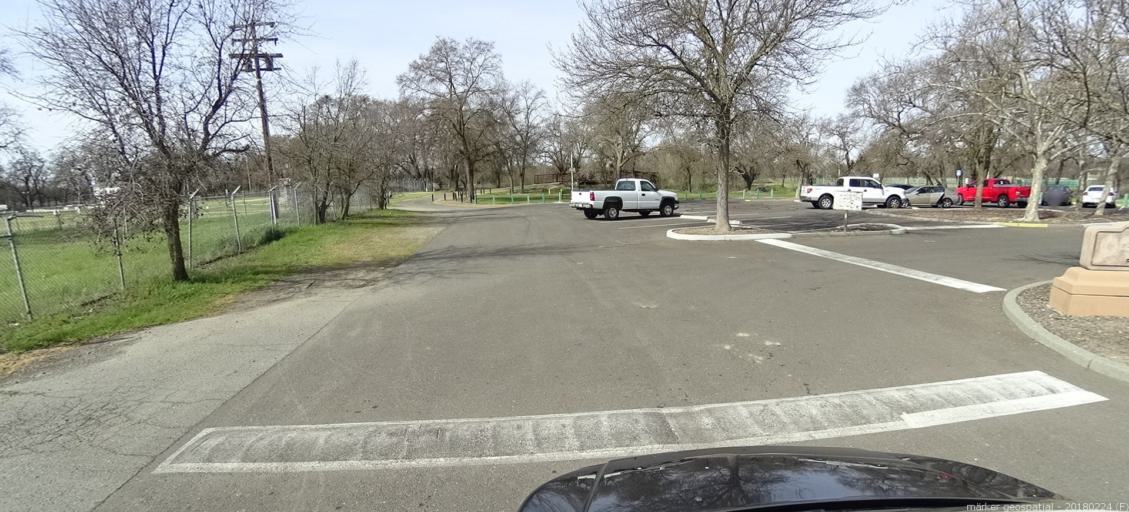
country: US
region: California
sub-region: Sacramento County
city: Rio Linda
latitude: 38.6802
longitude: -121.4454
